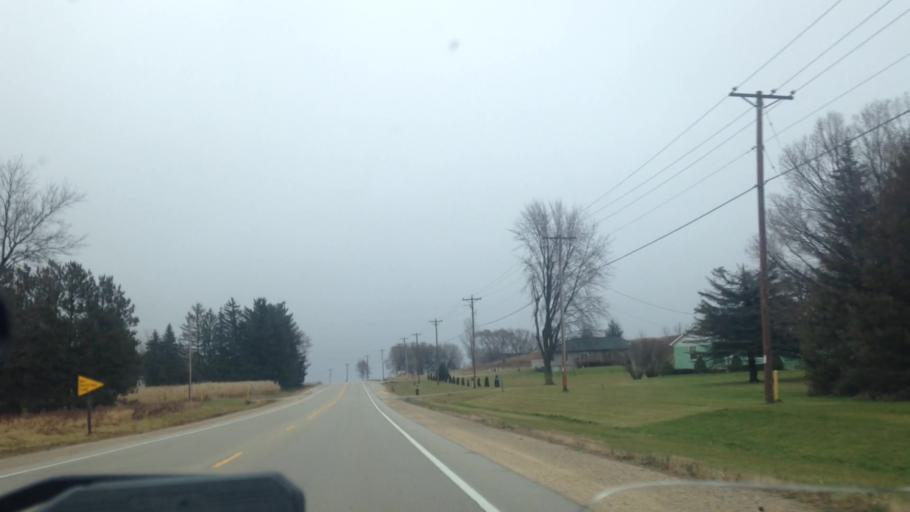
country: US
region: Wisconsin
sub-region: Dodge County
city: Beaver Dam
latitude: 43.4479
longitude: -88.7844
